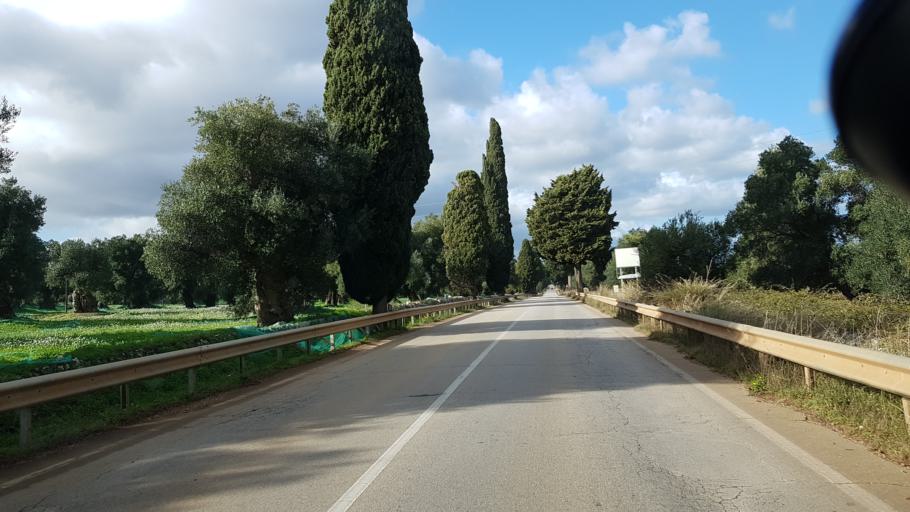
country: IT
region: Apulia
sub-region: Provincia di Brindisi
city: Ostuni
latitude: 40.7524
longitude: 17.5470
